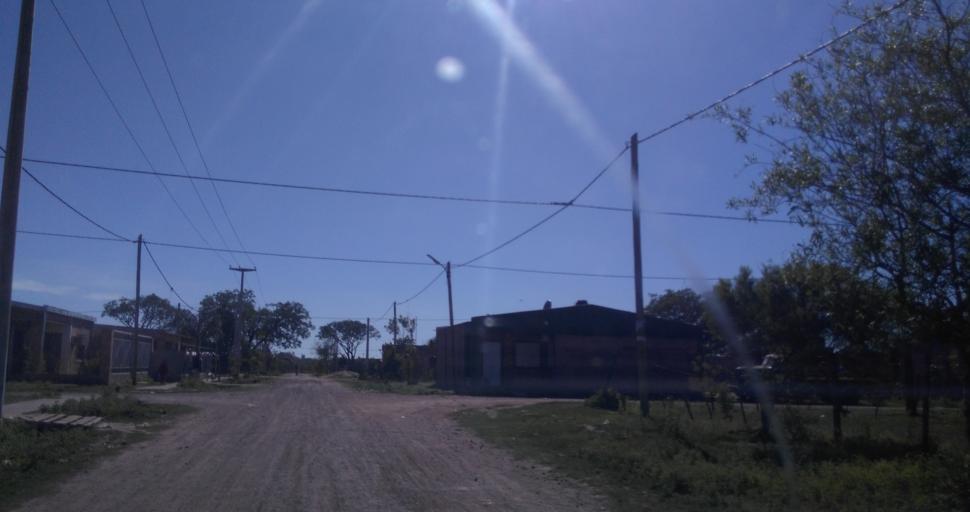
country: AR
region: Chaco
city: Fontana
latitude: -27.4178
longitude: -59.0206
